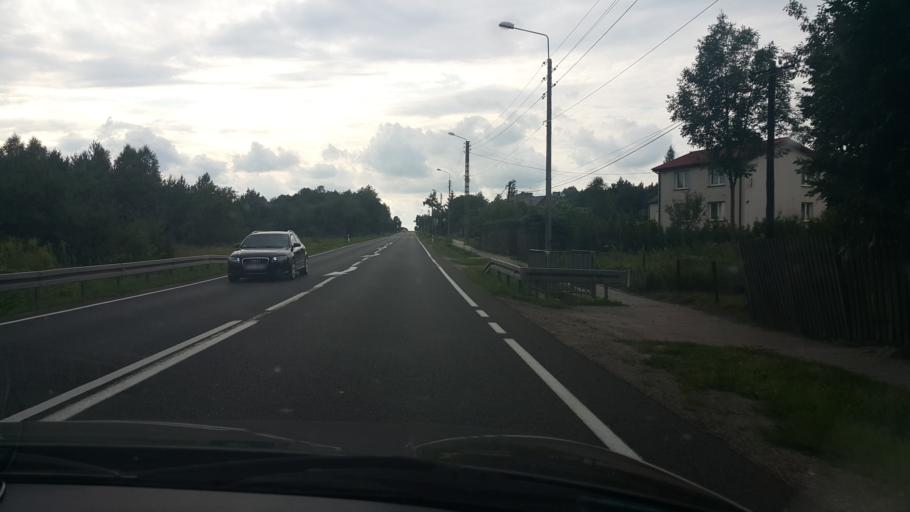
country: PL
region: Swietokrzyskie
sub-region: Powiat skarzyski
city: Blizyn
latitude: 51.1010
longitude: 20.7885
